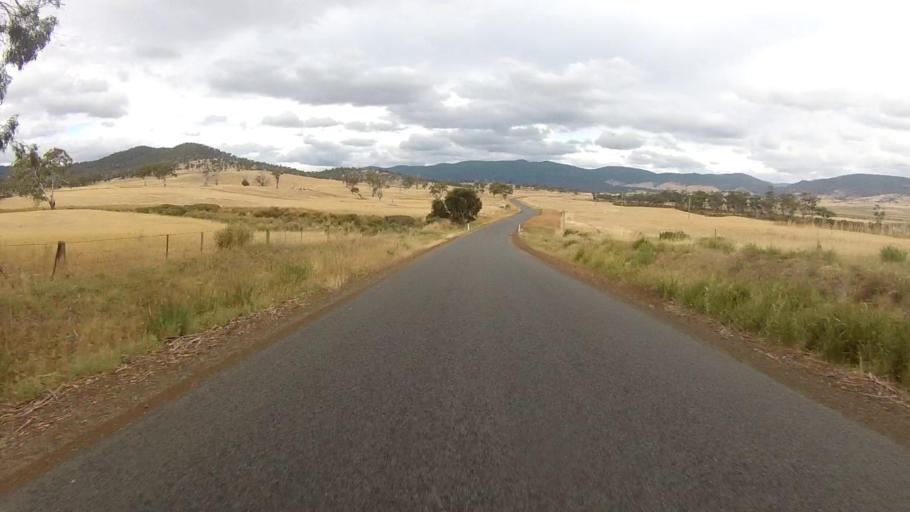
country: AU
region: Tasmania
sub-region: Northern Midlands
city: Evandale
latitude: -41.7951
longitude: 147.7456
